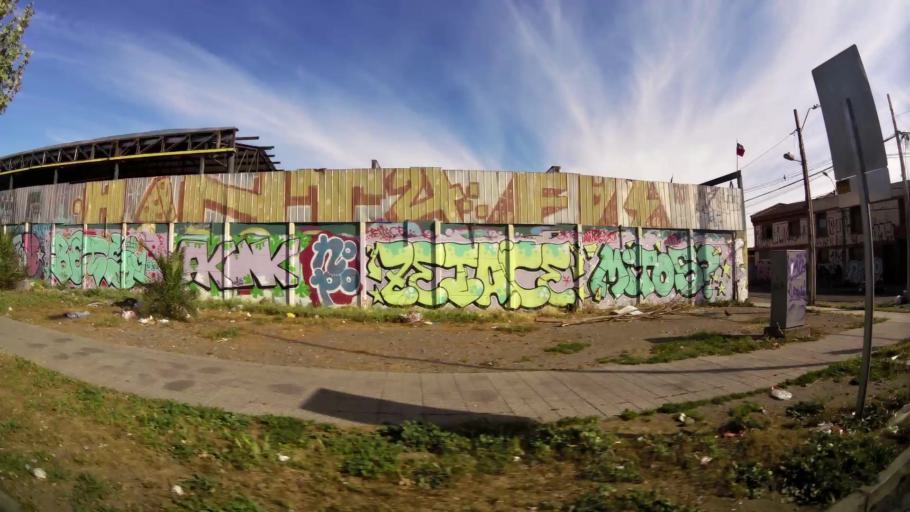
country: CL
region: Santiago Metropolitan
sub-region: Provincia de Santiago
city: Santiago
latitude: -33.4593
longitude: -70.6852
